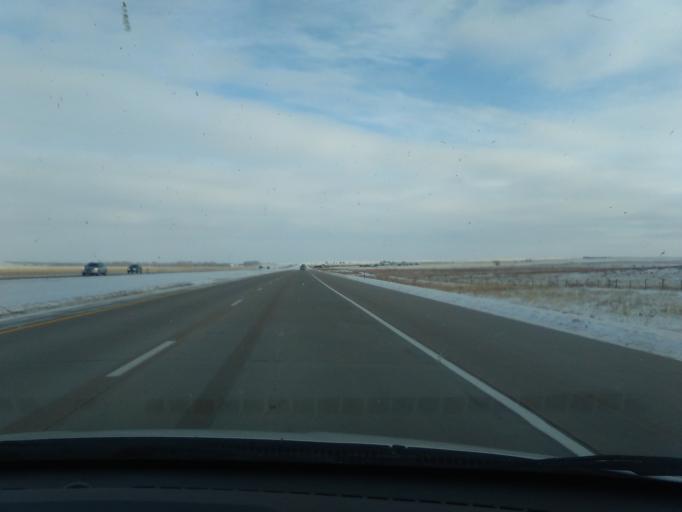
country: US
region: Nebraska
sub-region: Deuel County
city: Chappell
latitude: 41.1064
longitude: -102.5498
